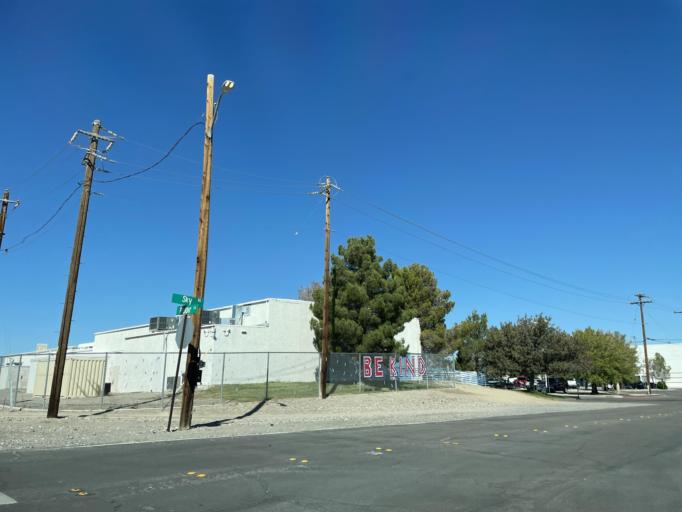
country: US
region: Nevada
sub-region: Nye County
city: Pahrump
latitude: 36.5734
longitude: -115.6755
